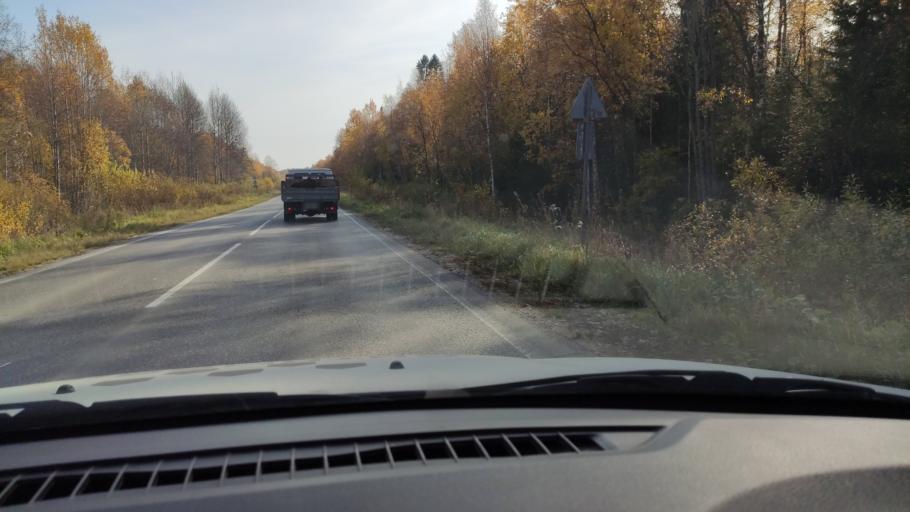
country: RU
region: Perm
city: Novyye Lyady
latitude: 58.0261
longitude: 56.6318
